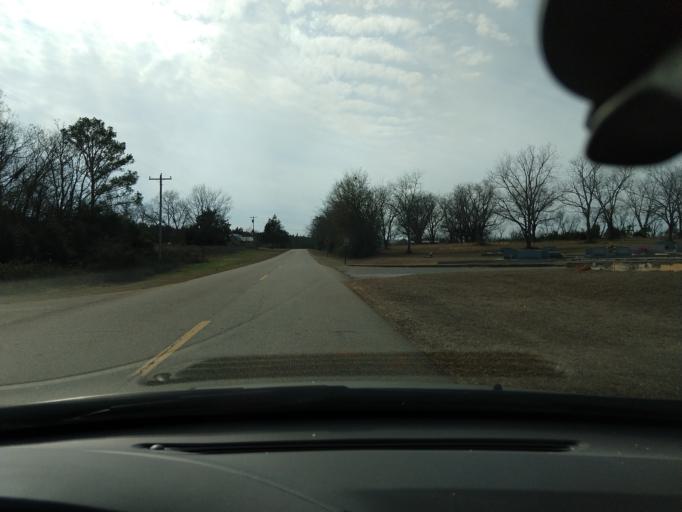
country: US
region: Georgia
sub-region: Webster County
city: Preston
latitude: 32.0283
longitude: -84.4220
